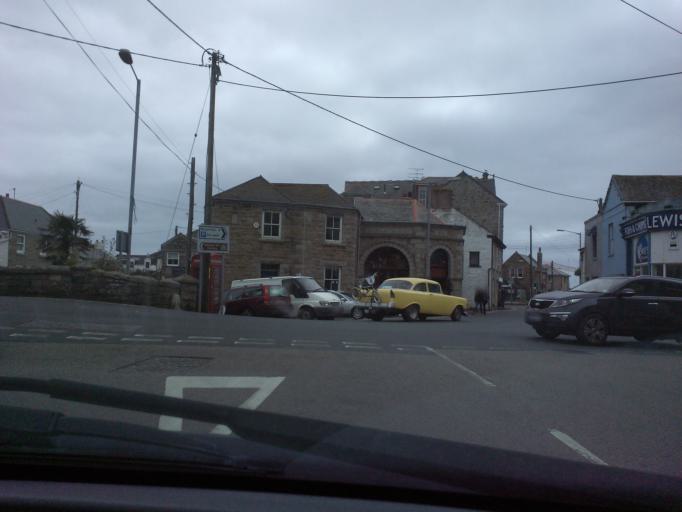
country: GB
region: England
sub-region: Cornwall
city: Penzance
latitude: 50.1068
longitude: -5.5505
